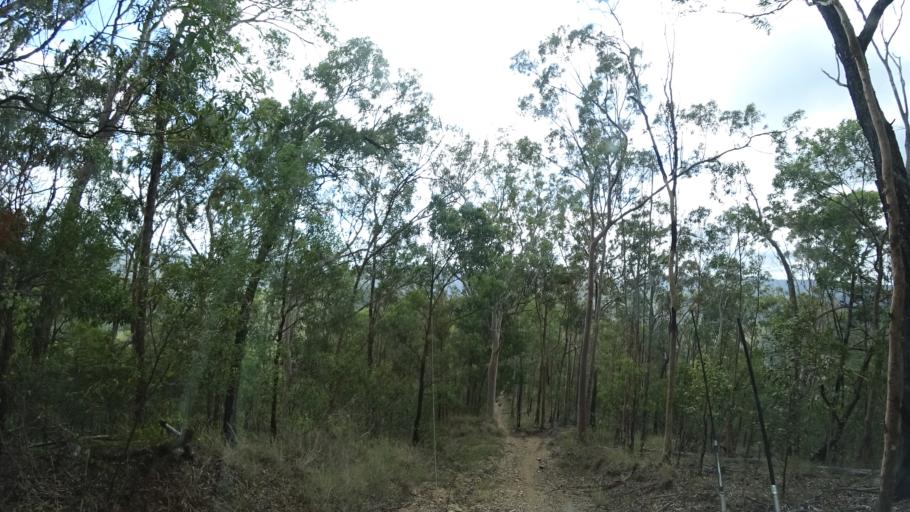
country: AU
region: Queensland
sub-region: Moreton Bay
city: Highvale
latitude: -27.3780
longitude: 152.7378
